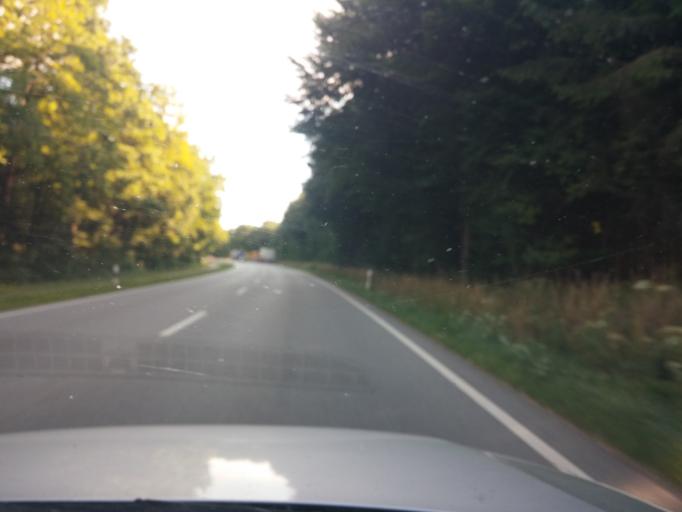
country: DE
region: Bavaria
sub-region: Upper Bavaria
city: Haar
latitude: 48.0928
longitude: 11.7239
